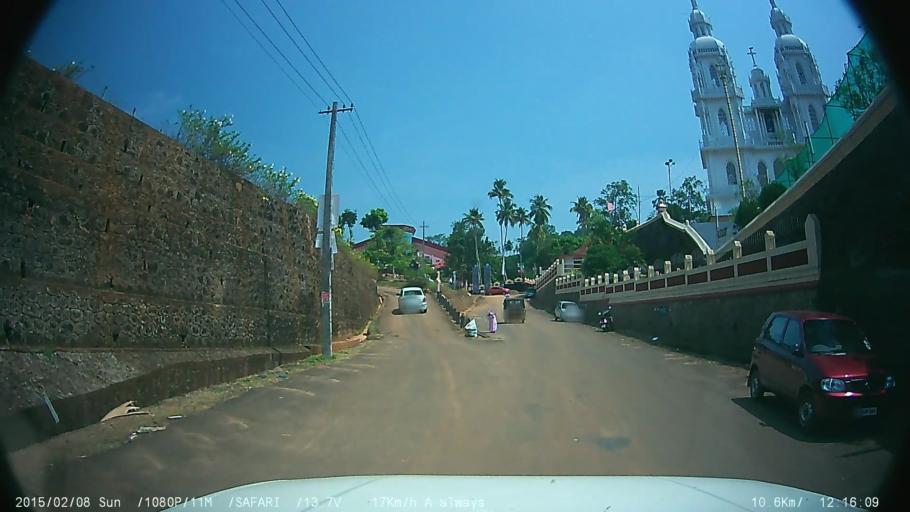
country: IN
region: Kerala
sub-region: Kottayam
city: Palackattumala
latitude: 9.7546
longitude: 76.5640
